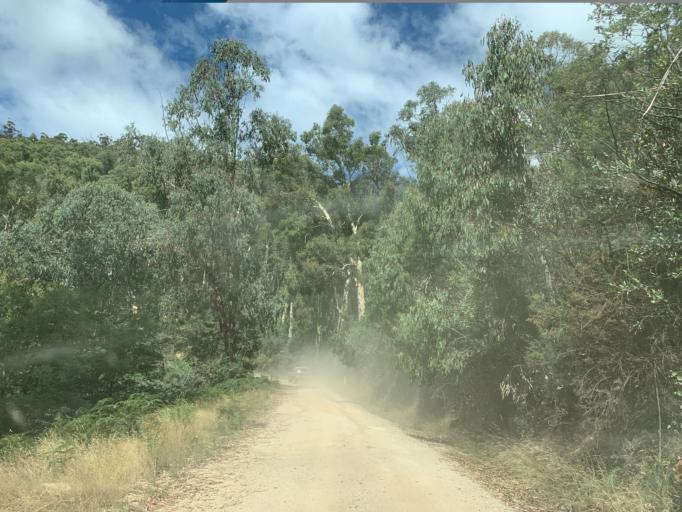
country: AU
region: Victoria
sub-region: Mansfield
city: Mansfield
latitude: -37.0928
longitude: 146.5290
